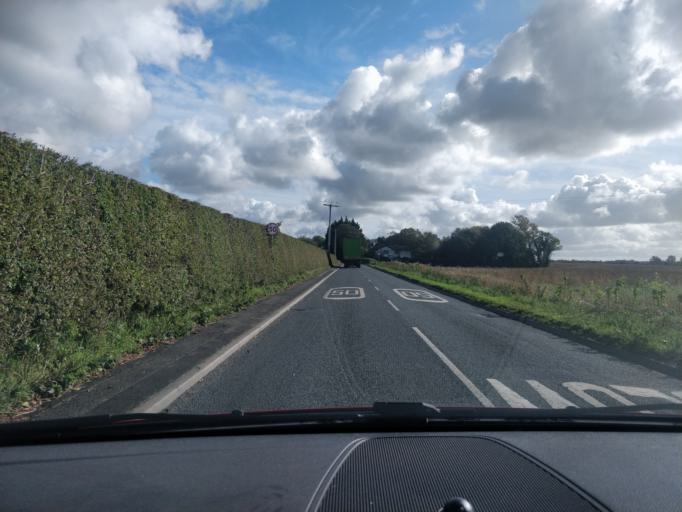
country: GB
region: England
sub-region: Lancashire
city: Ormskirk
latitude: 53.5922
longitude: -2.8899
